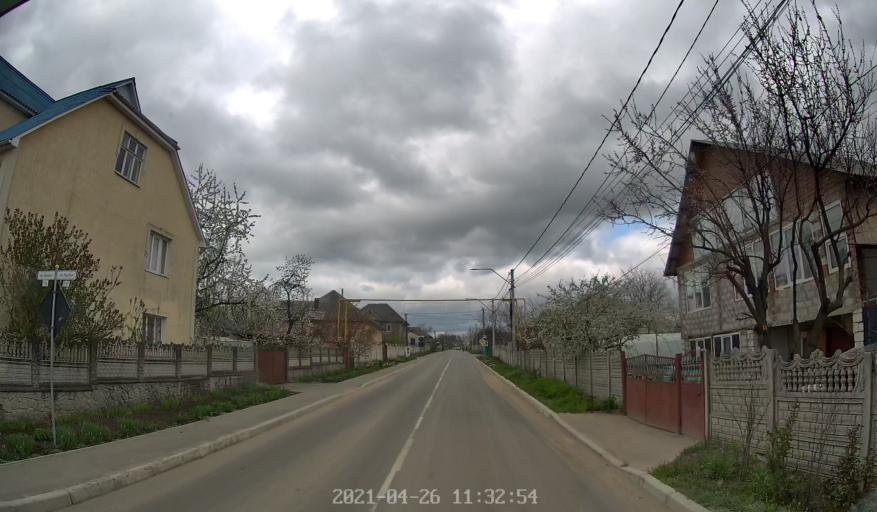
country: MD
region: Chisinau
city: Ciorescu
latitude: 47.1306
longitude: 28.9003
